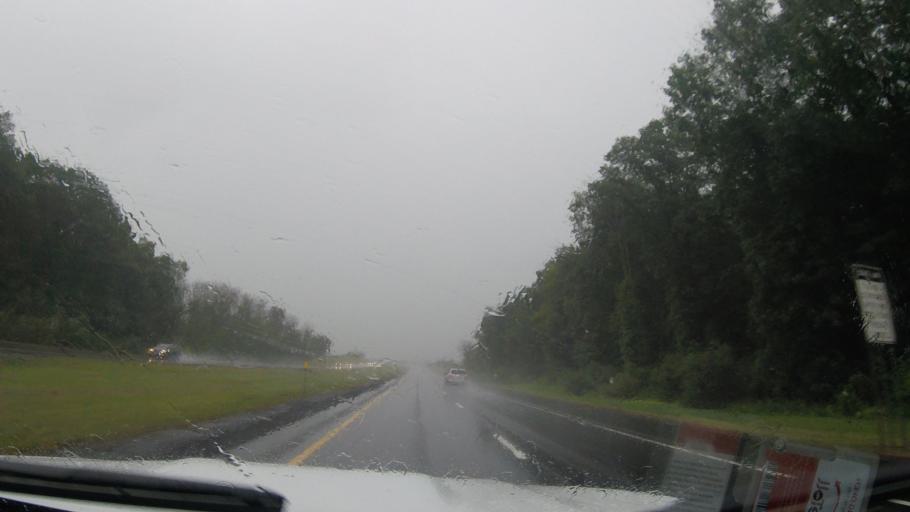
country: US
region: New York
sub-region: Seneca County
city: Waterloo
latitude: 42.9589
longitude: -76.9347
